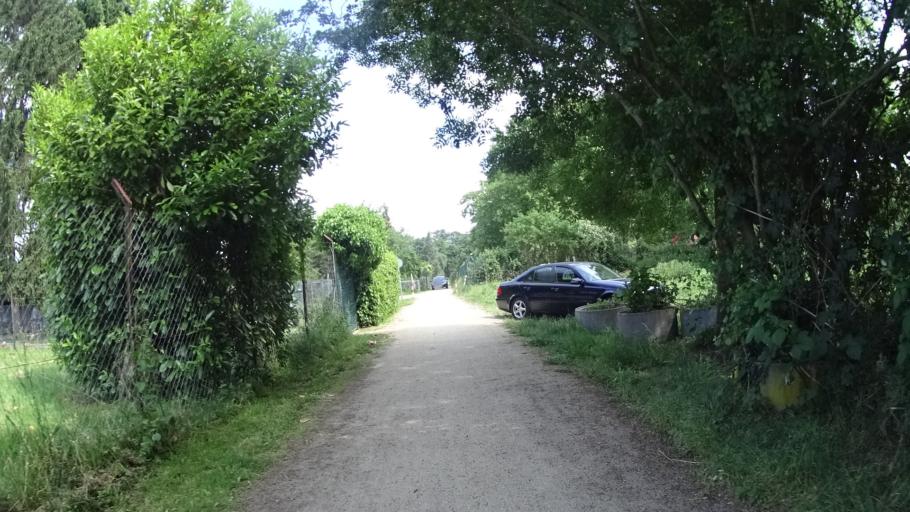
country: DE
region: Hesse
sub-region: Regierungsbezirk Darmstadt
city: Offenbach
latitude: 50.1110
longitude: 8.7845
